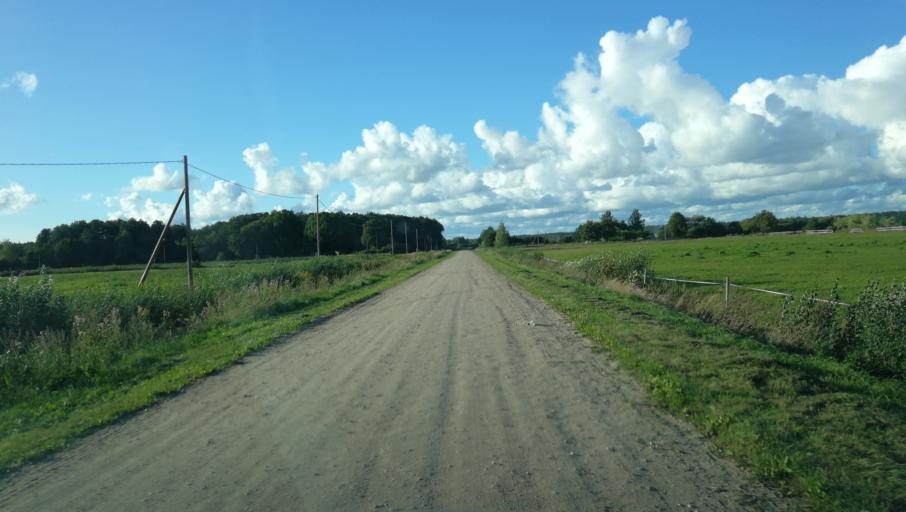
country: LV
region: Riga
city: Jaunciems
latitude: 57.0726
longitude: 24.2334
